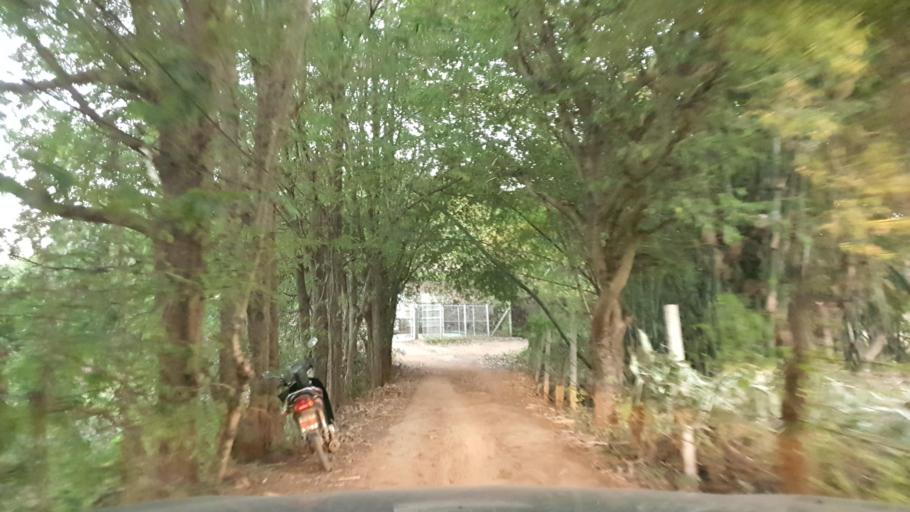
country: TH
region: Chiang Mai
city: Mae Wang
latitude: 18.6966
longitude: 98.8149
